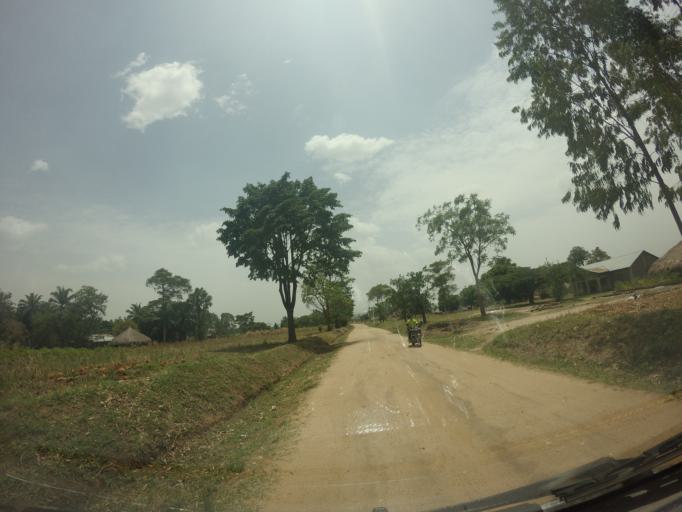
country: UG
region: Northern Region
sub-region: Arua District
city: Arua
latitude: 2.9467
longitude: 30.9131
